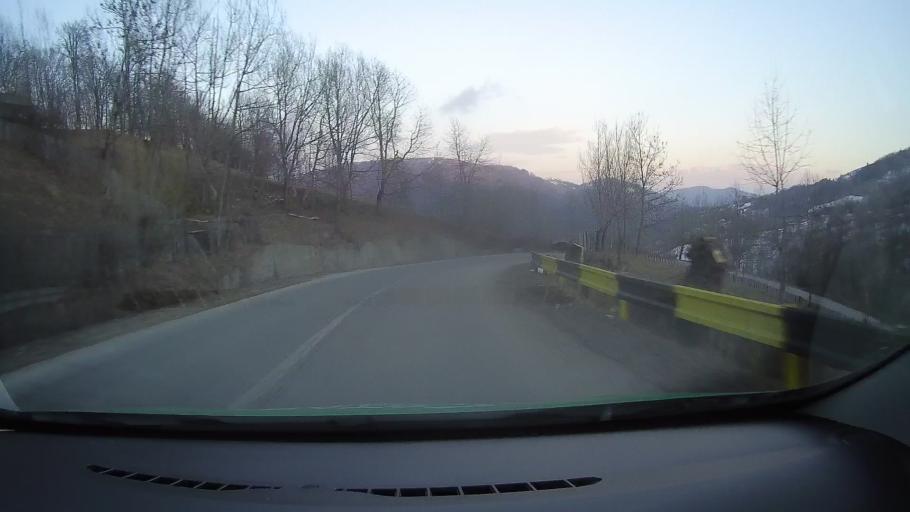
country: RO
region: Prahova
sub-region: Comuna Secaria
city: Secaria
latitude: 45.2695
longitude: 25.6787
